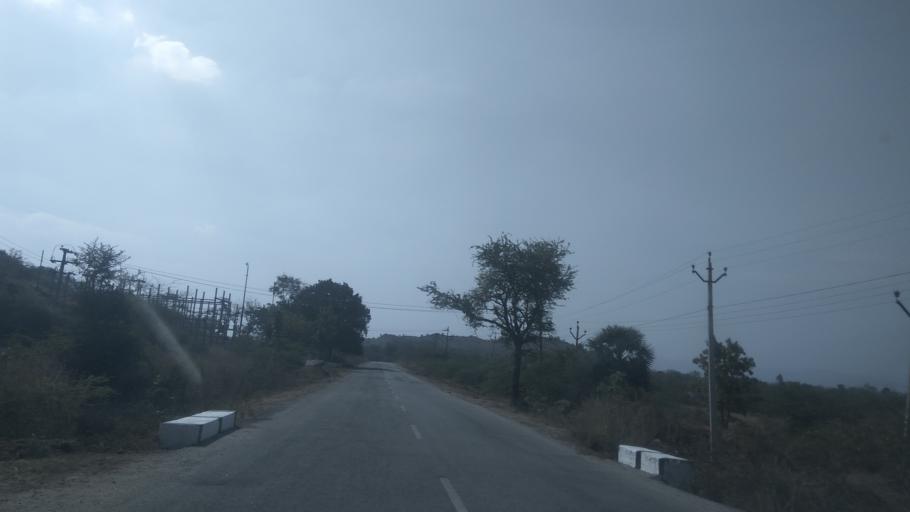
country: IN
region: Andhra Pradesh
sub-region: Chittoor
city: Renigunta
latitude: 13.5527
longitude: 79.5027
